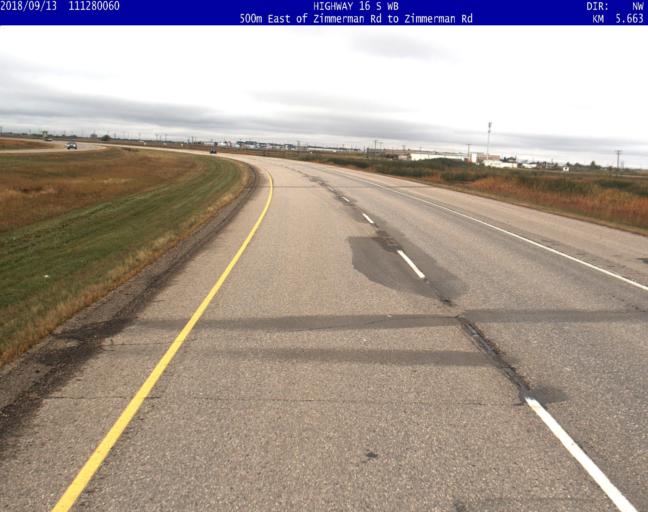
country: CA
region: Saskatchewan
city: Saskatoon
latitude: 52.0841
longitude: -106.5167
